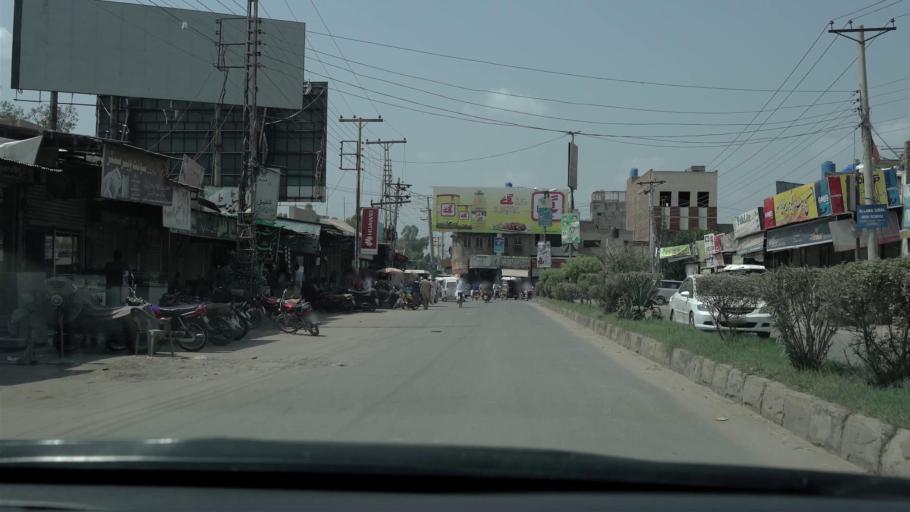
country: PK
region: Punjab
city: Gojra
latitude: 31.1516
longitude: 72.6781
